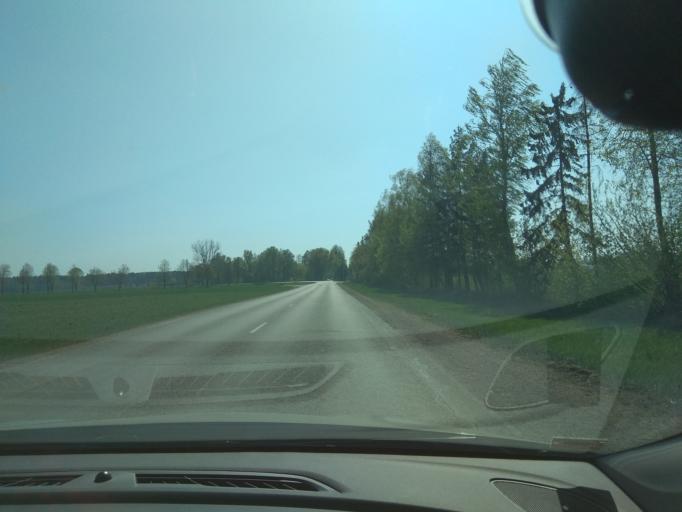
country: LT
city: Linkuva
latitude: 56.0060
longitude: 24.1620
